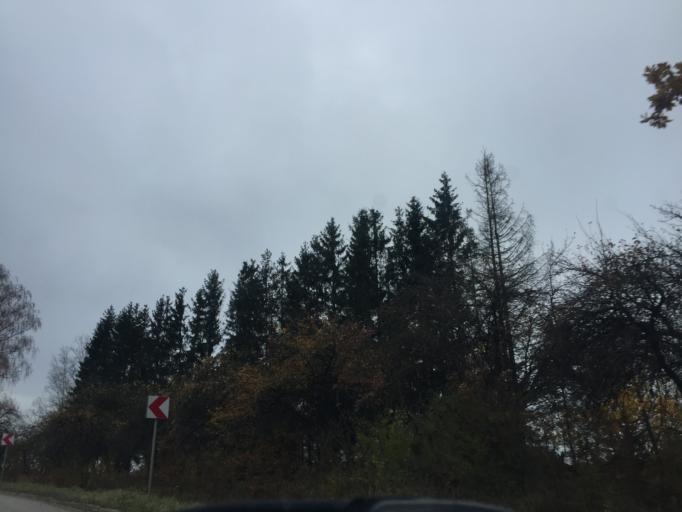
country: LV
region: Broceni
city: Broceni
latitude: 56.6724
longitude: 22.5201
